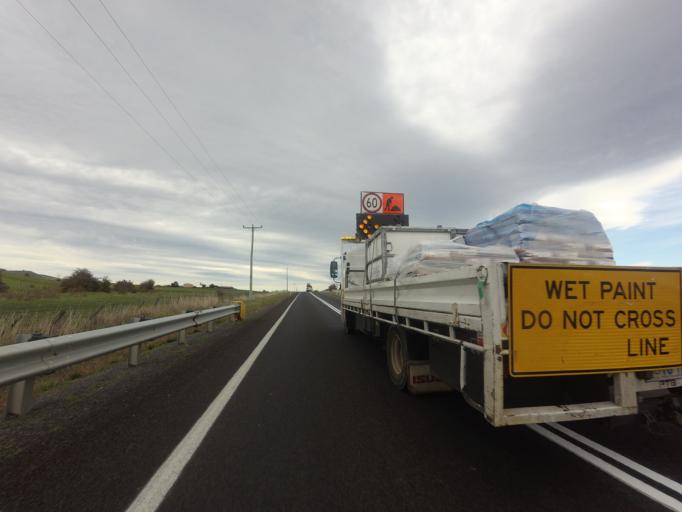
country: AU
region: Tasmania
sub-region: Derwent Valley
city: New Norfolk
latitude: -42.4926
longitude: 146.7284
